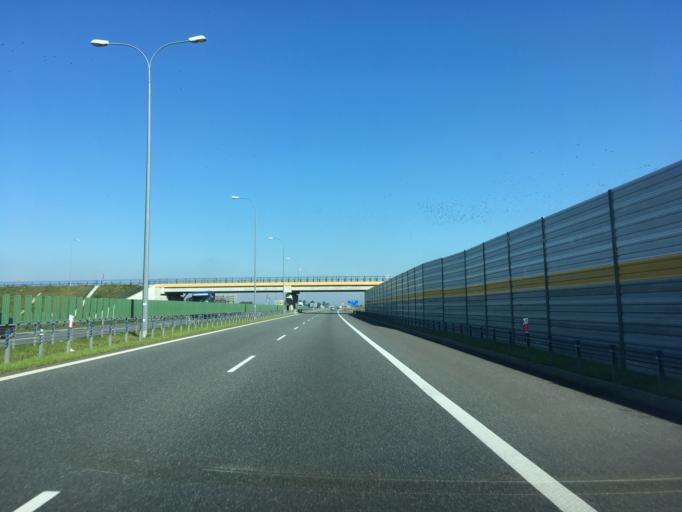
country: PL
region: Kujawsko-Pomorskie
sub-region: Powiat chelminski
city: Lisewo
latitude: 53.2914
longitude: 18.7079
